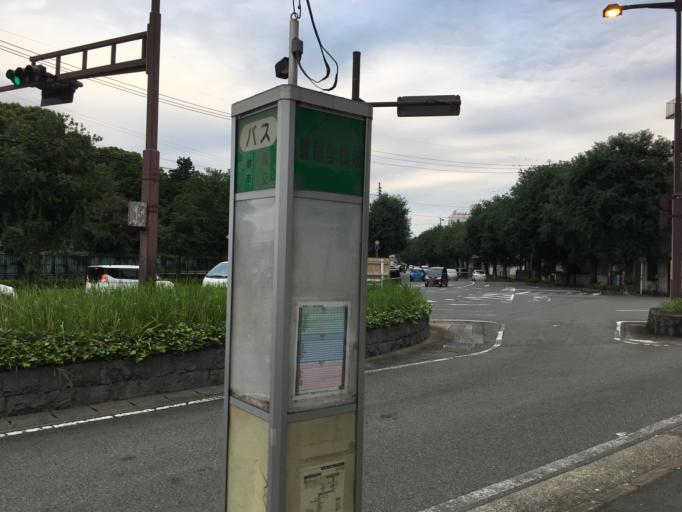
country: JP
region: Kumamoto
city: Kumamoto
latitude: 32.8067
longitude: 130.7290
